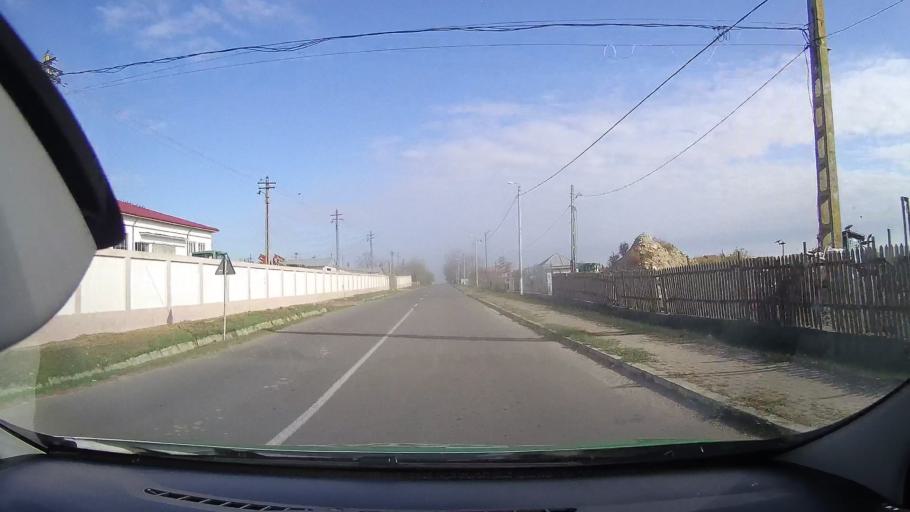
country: RO
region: Tulcea
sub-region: Comuna Mahmudia
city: Mahmudia
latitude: 45.0797
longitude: 29.0797
